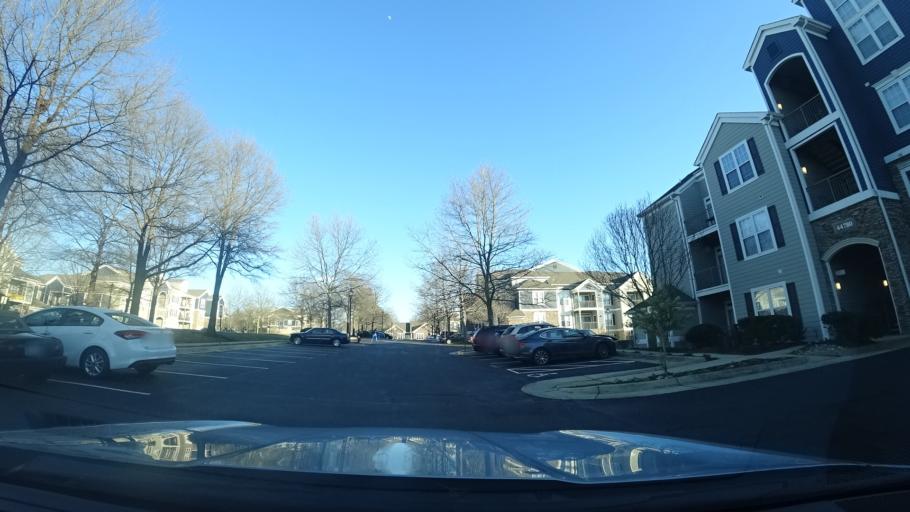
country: US
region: Virginia
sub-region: Loudoun County
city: University Center
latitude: 39.0653
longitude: -77.4508
